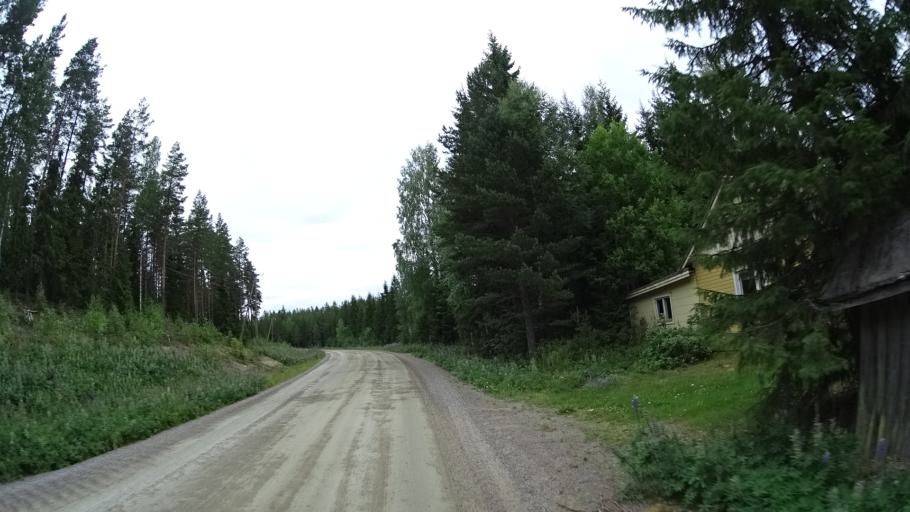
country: FI
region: Satakunta
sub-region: Pohjois-Satakunta
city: Jaemijaervi
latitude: 61.7744
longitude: 22.8617
